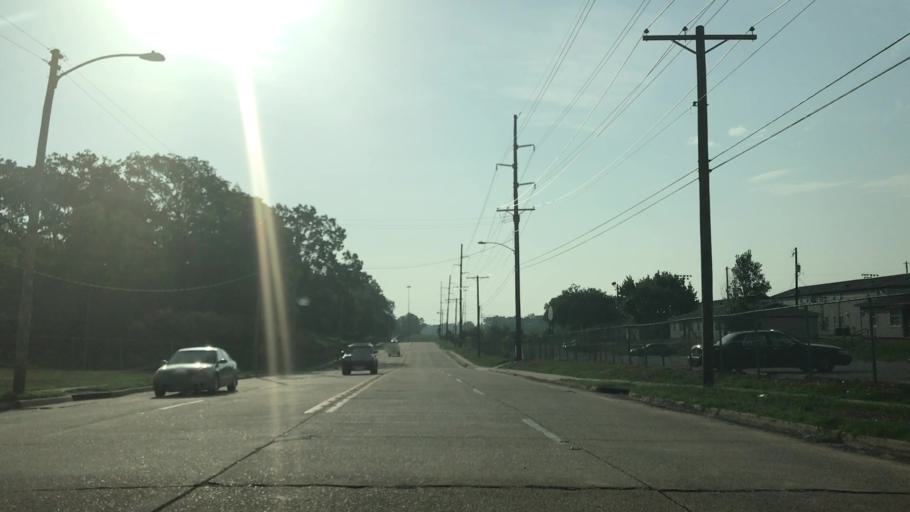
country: US
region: Louisiana
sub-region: Bossier Parish
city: Bossier City
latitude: 32.5000
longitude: -93.7223
